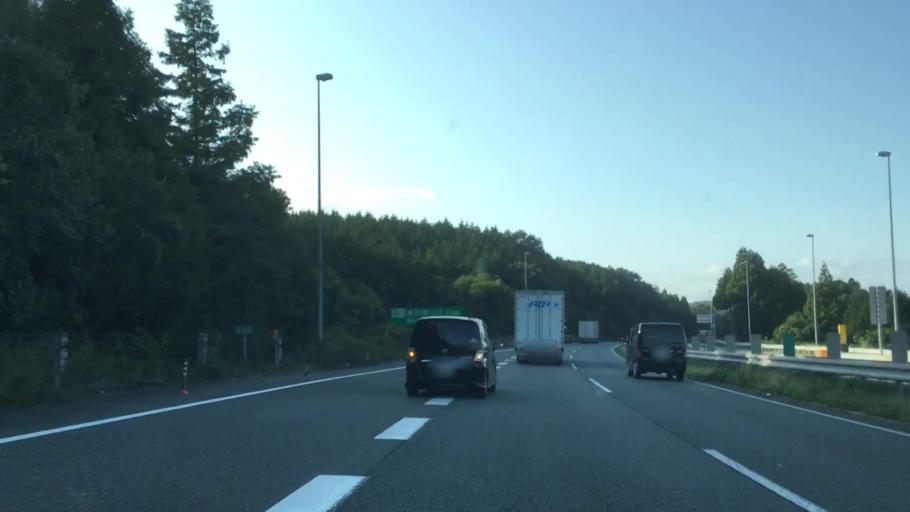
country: JP
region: Yamaguchi
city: Ogori-shimogo
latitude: 34.1550
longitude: 131.3346
